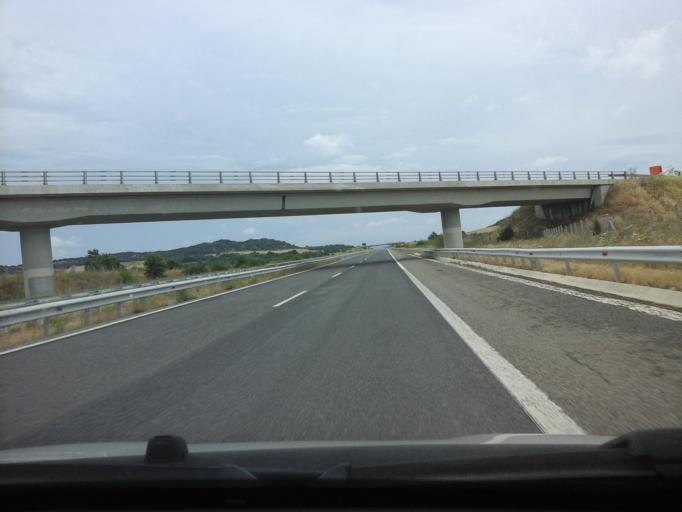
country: GR
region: East Macedonia and Thrace
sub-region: Nomos Evrou
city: Feres
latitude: 40.9205
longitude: 26.1317
